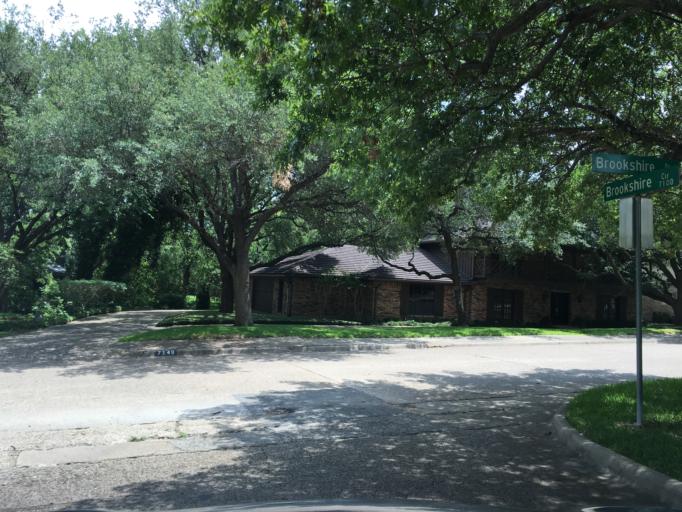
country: US
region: Texas
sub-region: Dallas County
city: University Park
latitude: 32.8934
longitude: -96.7804
